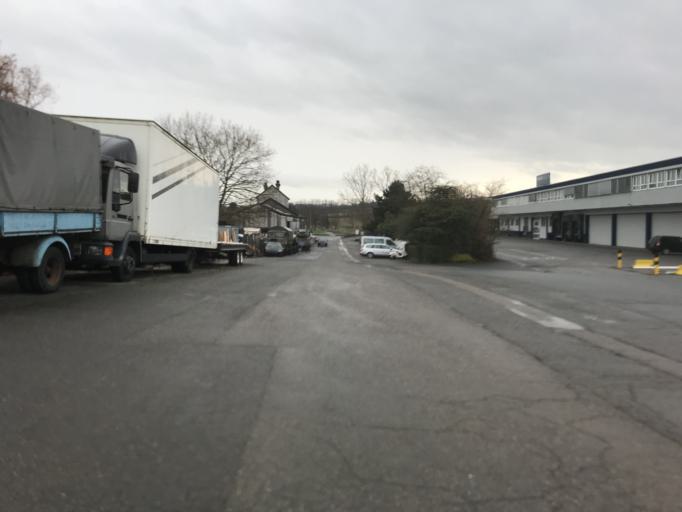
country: DE
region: Rheinland-Pfalz
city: Klein-Winternheim
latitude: 49.9631
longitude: 8.2218
